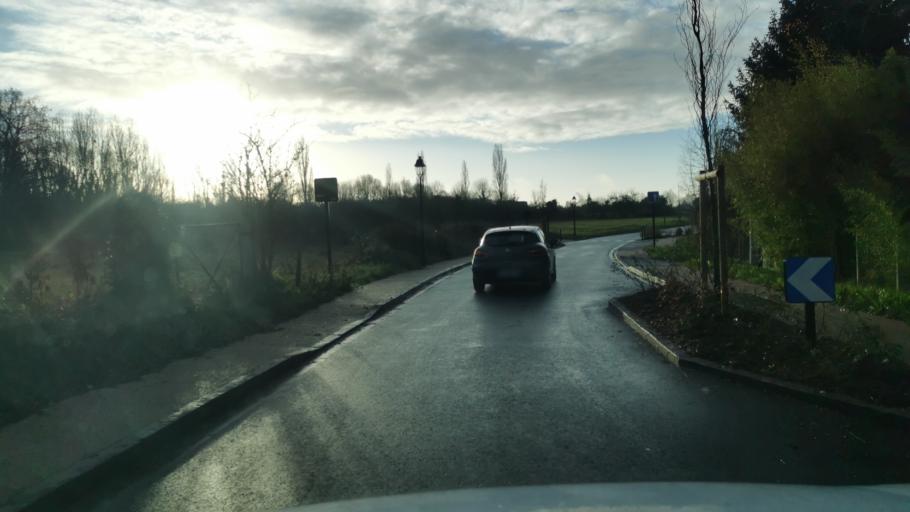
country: FR
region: Ile-de-France
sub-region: Departement des Yvelines
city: Bazainville
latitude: 48.8002
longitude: 1.6705
